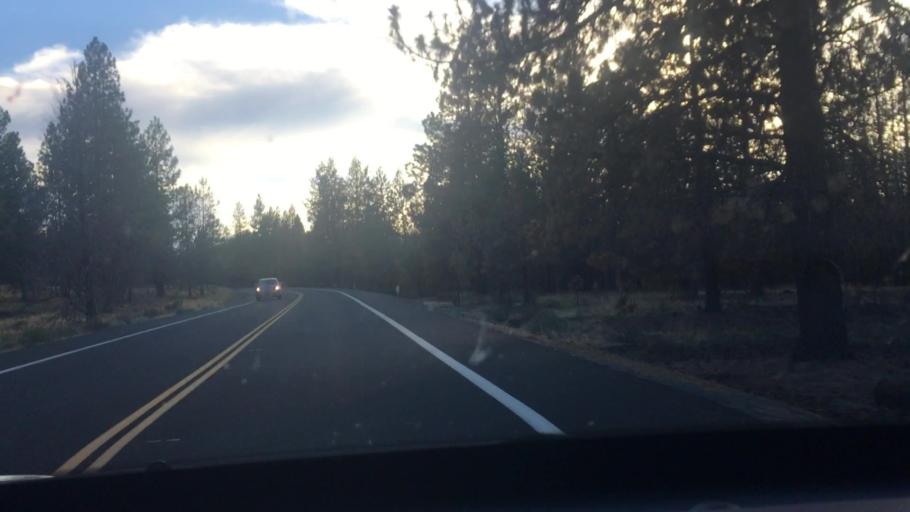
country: US
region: Oregon
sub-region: Deschutes County
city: Deschutes River Woods
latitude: 44.0492
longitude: -121.3886
